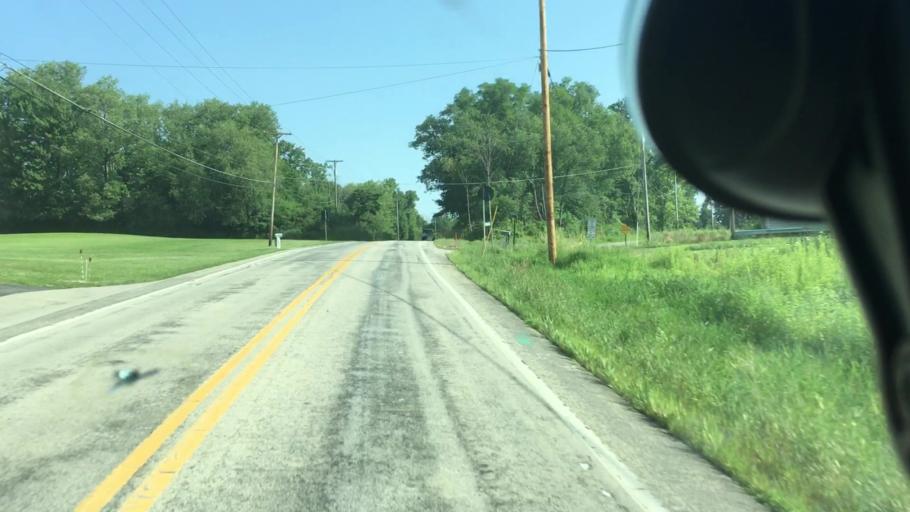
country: US
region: Pennsylvania
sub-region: Lawrence County
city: New Castle
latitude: 41.0005
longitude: -80.2703
